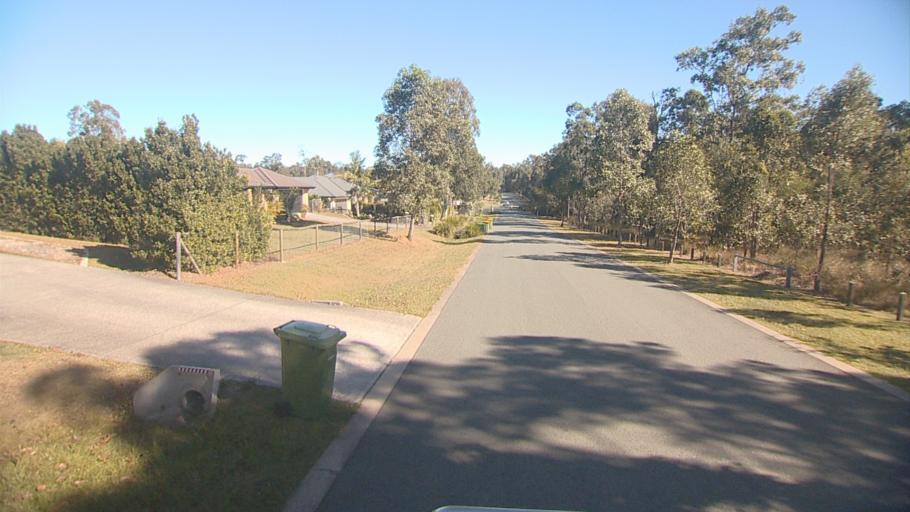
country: AU
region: Queensland
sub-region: Logan
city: North Maclean
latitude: -27.7555
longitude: 152.9670
